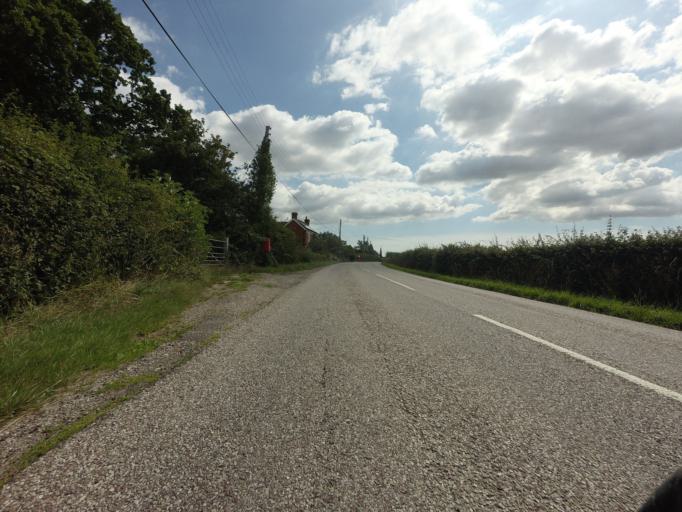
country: GB
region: England
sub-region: Kent
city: Stone
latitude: 51.0706
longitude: 0.7599
